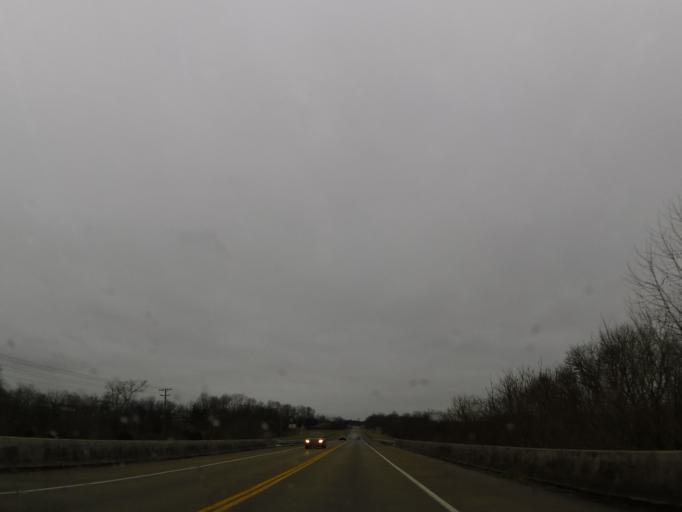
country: US
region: Kentucky
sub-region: Lincoln County
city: Stanford
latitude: 37.5348
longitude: -84.6418
